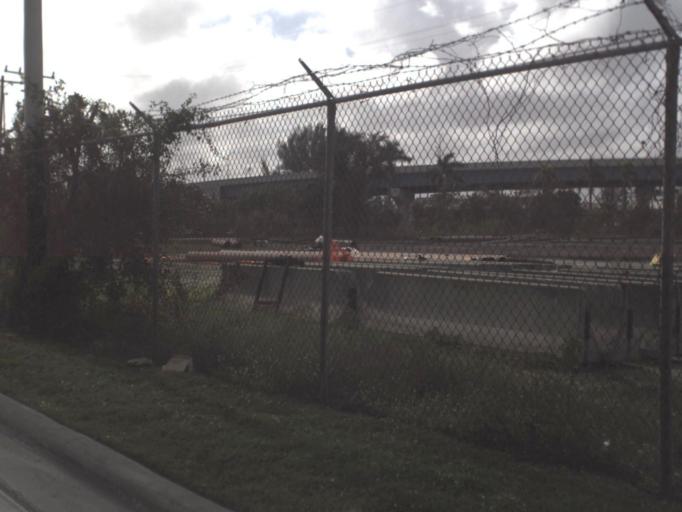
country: US
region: Florida
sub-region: Miami-Dade County
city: Virginia Gardens
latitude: 25.7980
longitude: -80.3067
